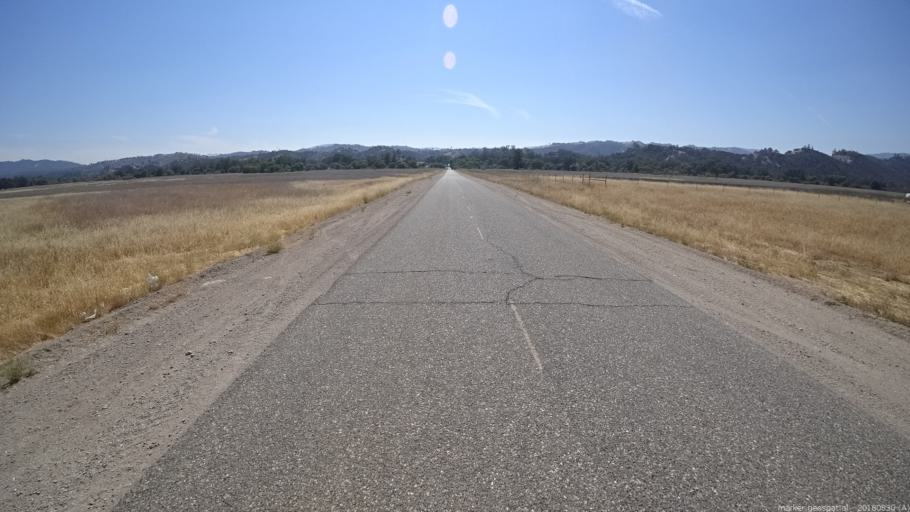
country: US
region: California
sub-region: Monterey County
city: King City
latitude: 36.0056
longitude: -121.2448
